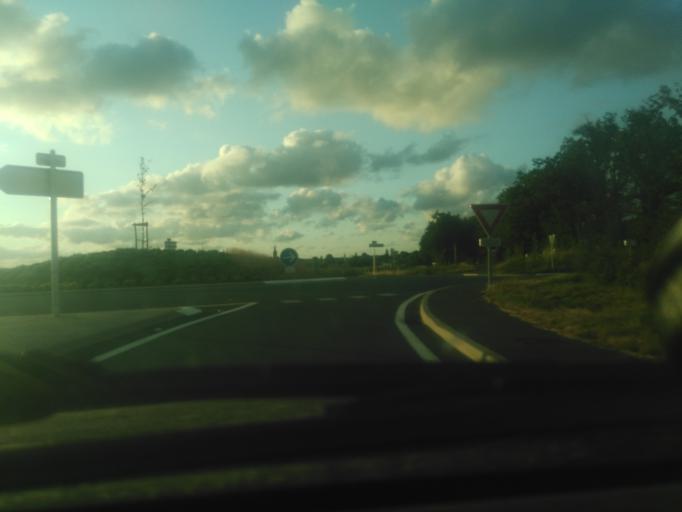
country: FR
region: Pays de la Loire
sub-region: Departement de la Vendee
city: La Ferriere
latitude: 46.7041
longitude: -1.3101
